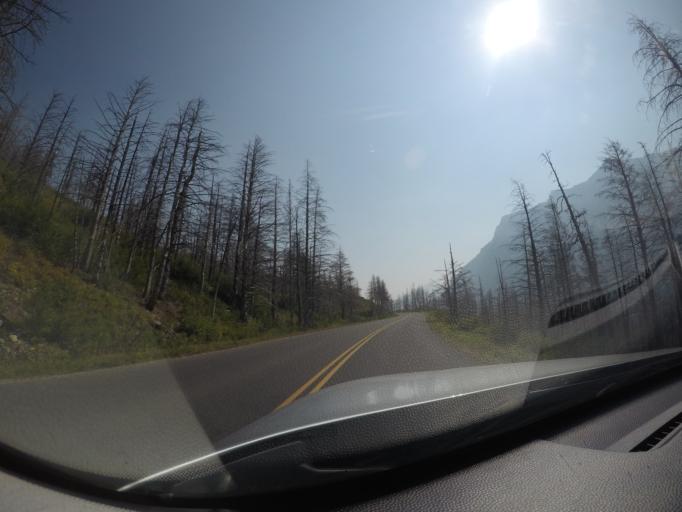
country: US
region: Montana
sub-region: Glacier County
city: Browning
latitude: 48.6848
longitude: -113.5682
